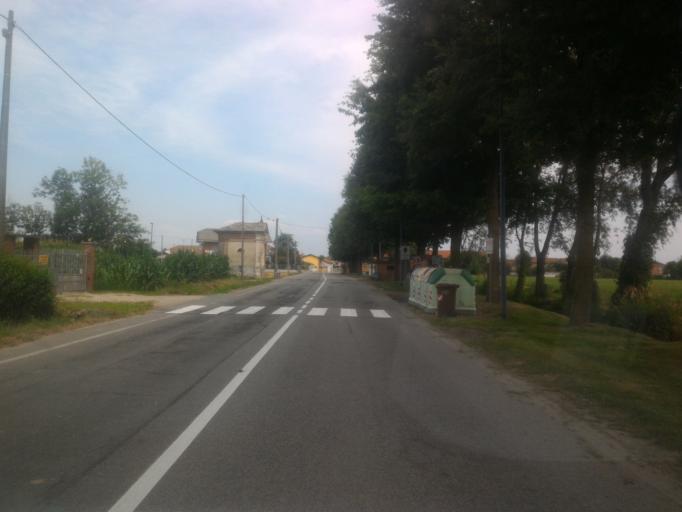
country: IT
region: Piedmont
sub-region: Provincia di Torino
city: Vigone
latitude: 44.8438
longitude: 7.4843
